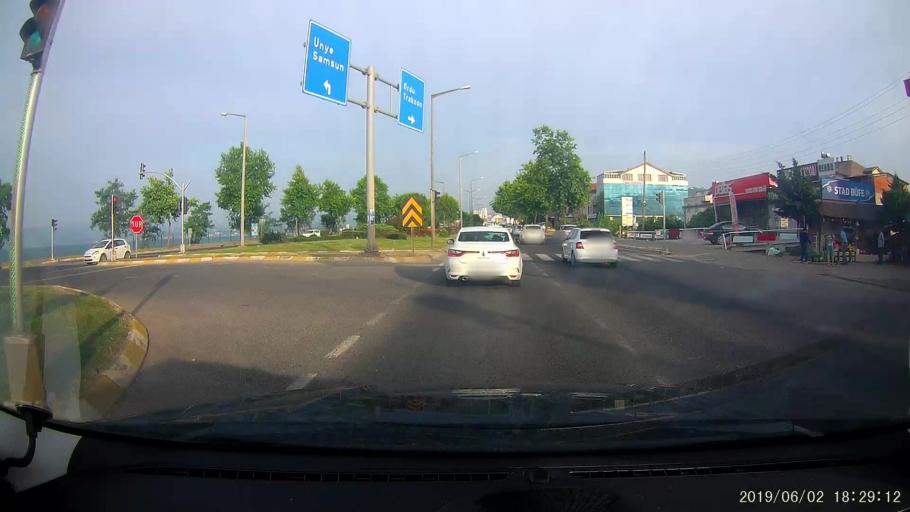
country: TR
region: Ordu
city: Fatsa
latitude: 41.0396
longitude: 37.4896
